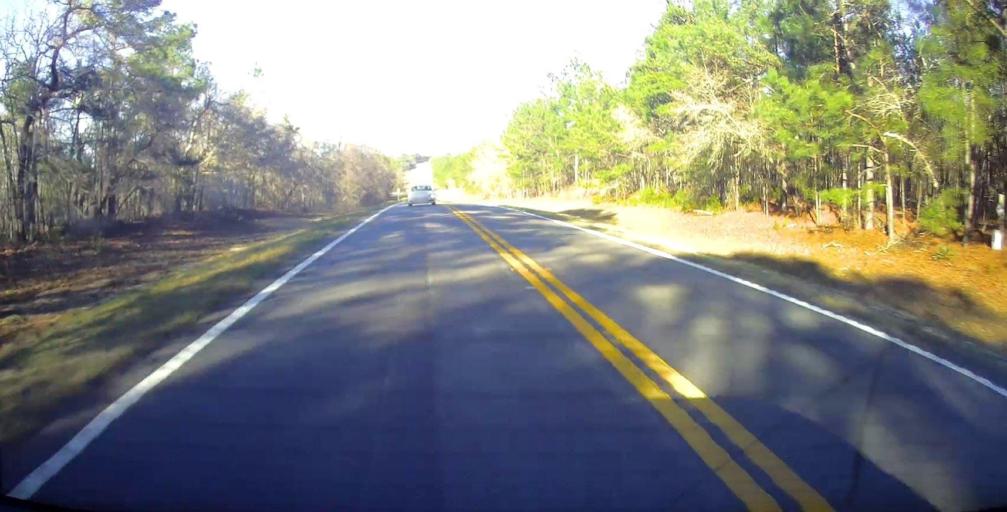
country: US
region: Georgia
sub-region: Taylor County
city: Butler
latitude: 32.5419
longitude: -84.2878
